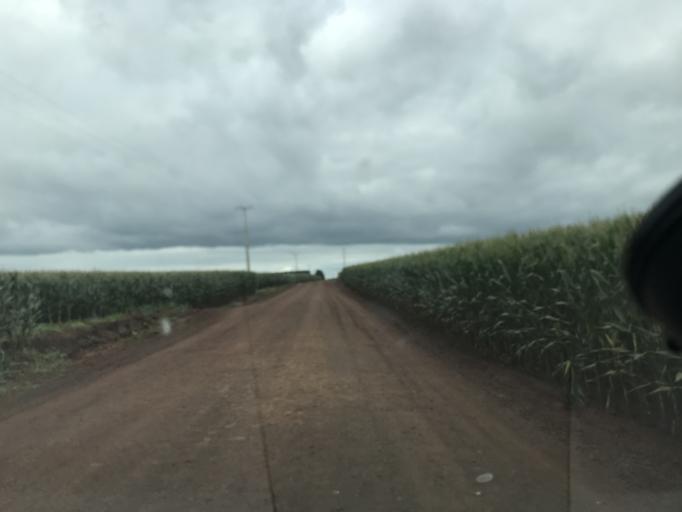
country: BR
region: Parana
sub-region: Palotina
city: Palotina
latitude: -24.2948
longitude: -53.8193
